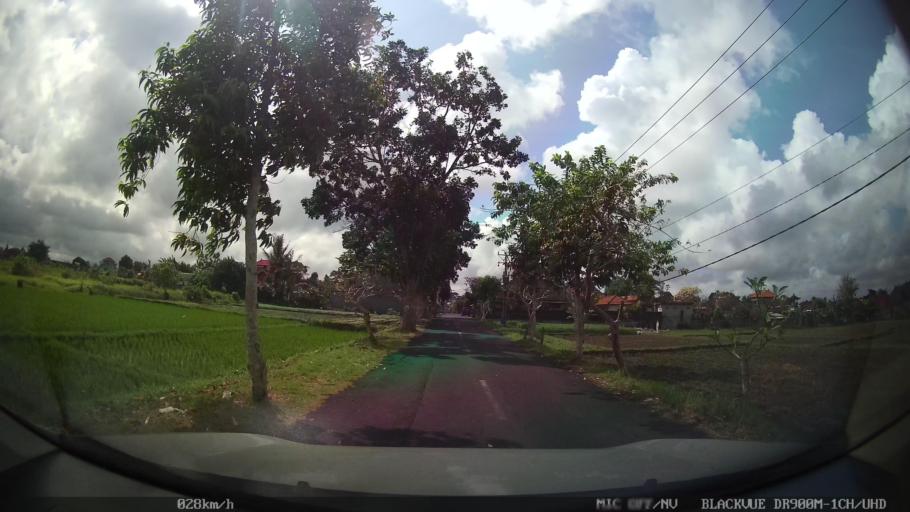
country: ID
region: Bali
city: Banjar Karangsuling
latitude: -8.6001
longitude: 115.1994
